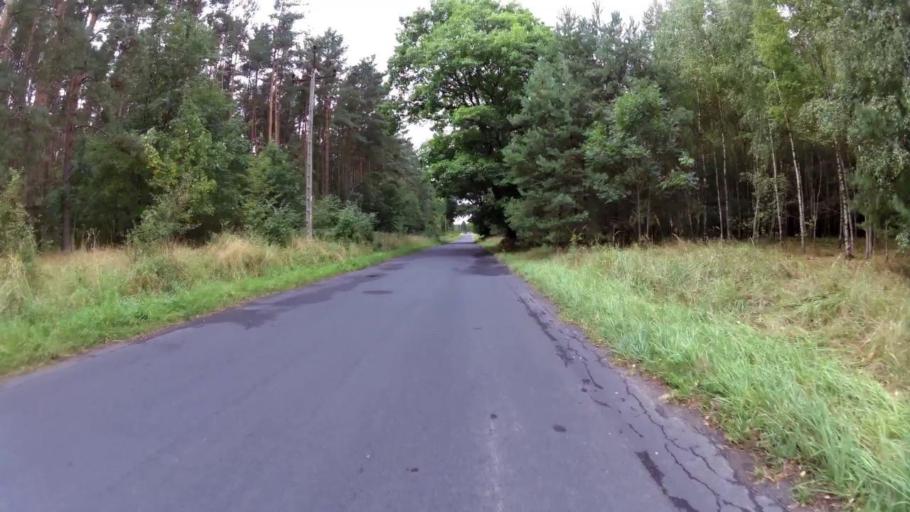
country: PL
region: West Pomeranian Voivodeship
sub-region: Powiat mysliborski
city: Debno
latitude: 52.8507
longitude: 14.7218
